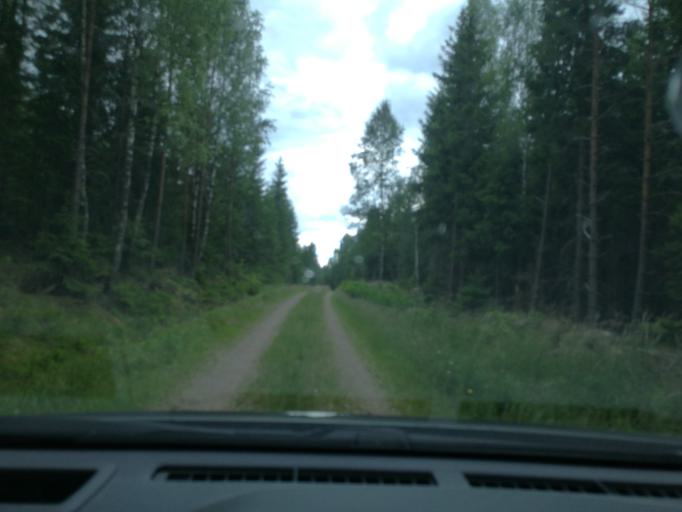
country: SE
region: Vaestmanland
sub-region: Surahammars Kommun
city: Ramnas
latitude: 59.8076
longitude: 16.3197
